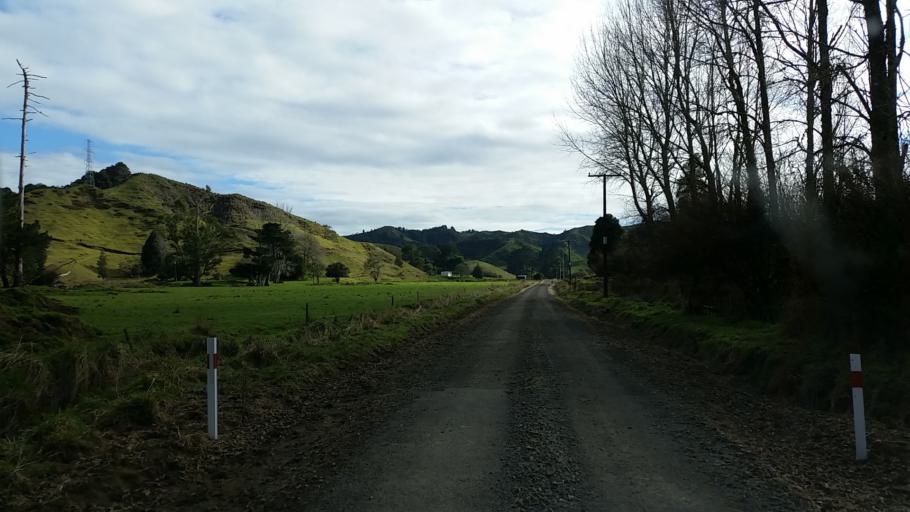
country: NZ
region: Taranaki
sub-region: South Taranaki District
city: Eltham
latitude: -39.2345
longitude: 174.5689
